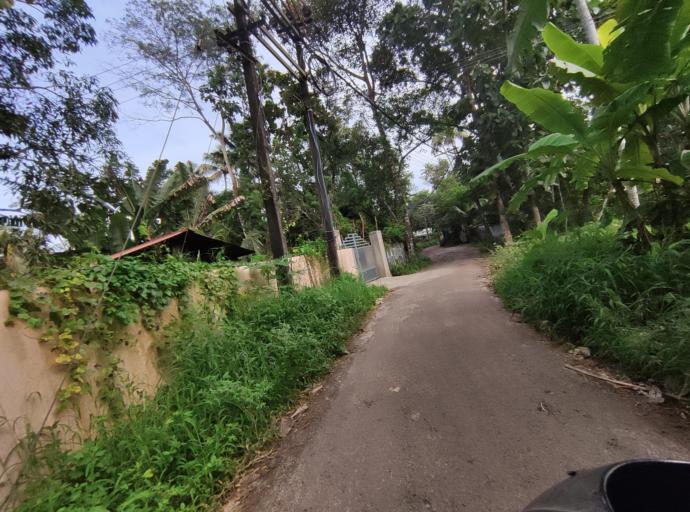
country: IN
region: Kerala
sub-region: Alappuzha
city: Vayalar
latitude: 9.6977
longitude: 76.3207
